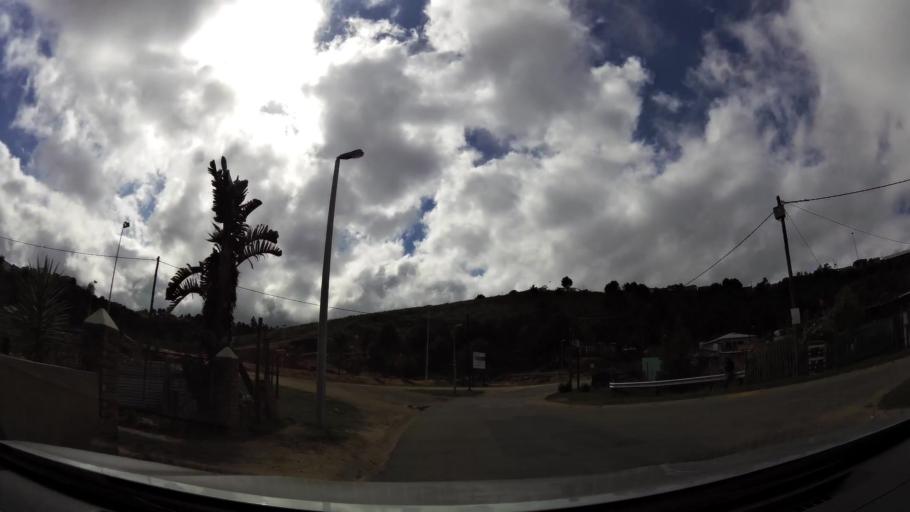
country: ZA
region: Western Cape
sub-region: Eden District Municipality
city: Knysna
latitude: -34.0335
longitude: 23.1028
